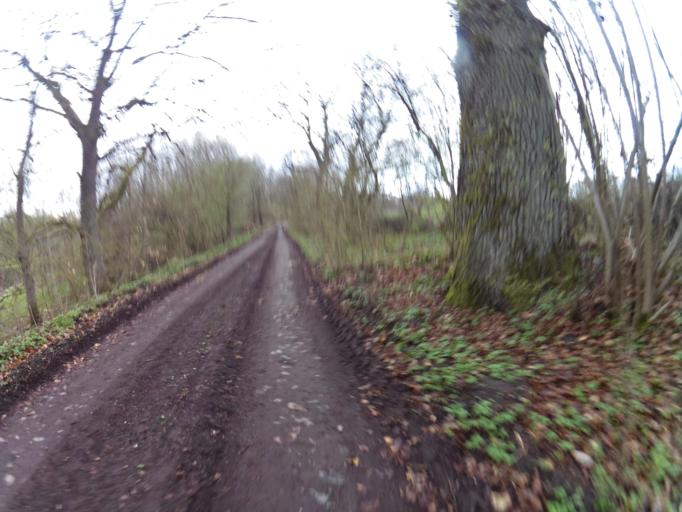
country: PL
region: West Pomeranian Voivodeship
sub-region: Powiat szczecinecki
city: Borne Sulinowo
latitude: 53.6480
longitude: 16.4998
